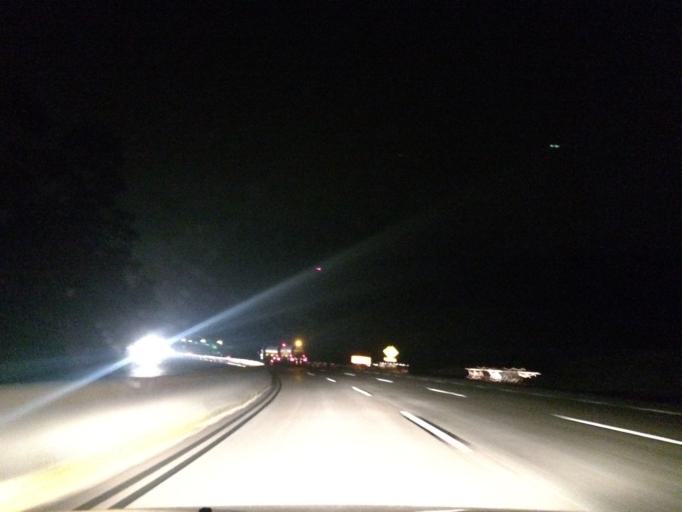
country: MX
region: Mexico
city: Rio Frio de Juarez
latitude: 19.3365
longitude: -98.7103
